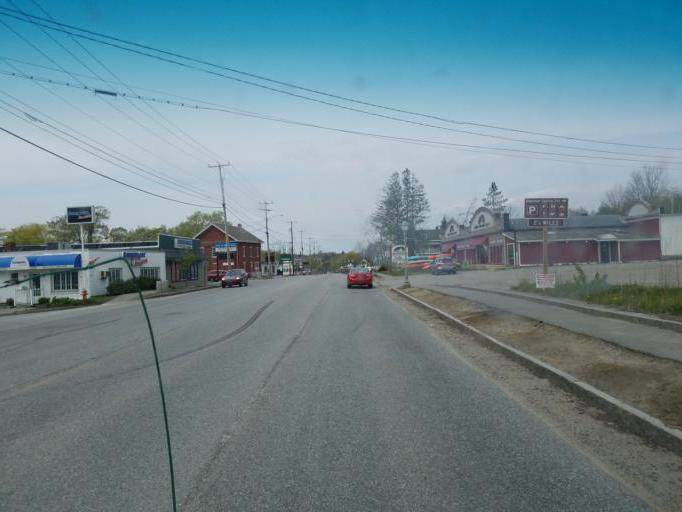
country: US
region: Maine
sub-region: Hancock County
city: Ellsworth
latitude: 44.5410
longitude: -68.4177
